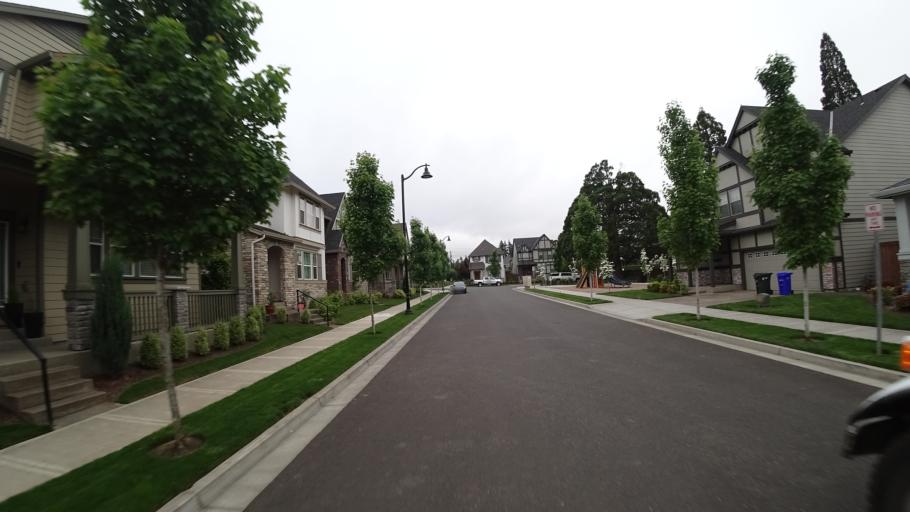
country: US
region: Oregon
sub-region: Washington County
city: Rockcreek
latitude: 45.5246
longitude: -122.9014
